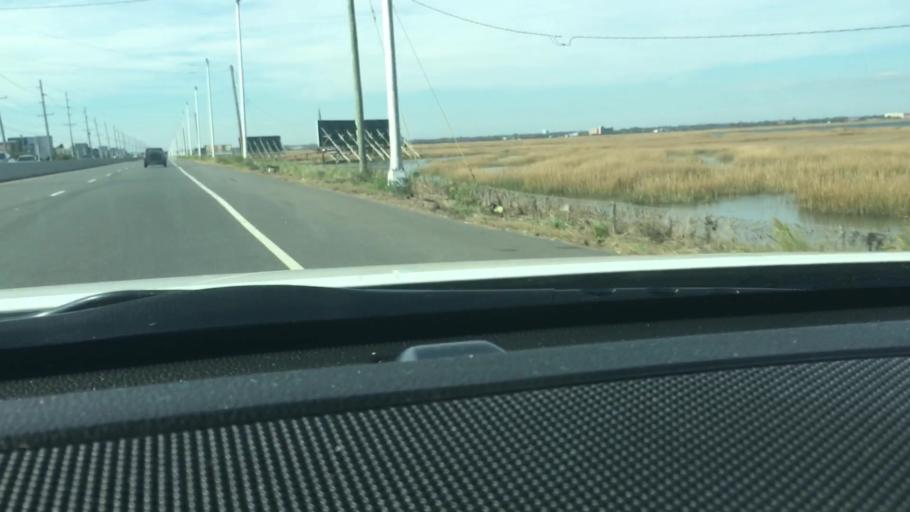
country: US
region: New Jersey
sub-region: Atlantic County
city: Ventnor City
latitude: 39.3864
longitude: -74.4660
